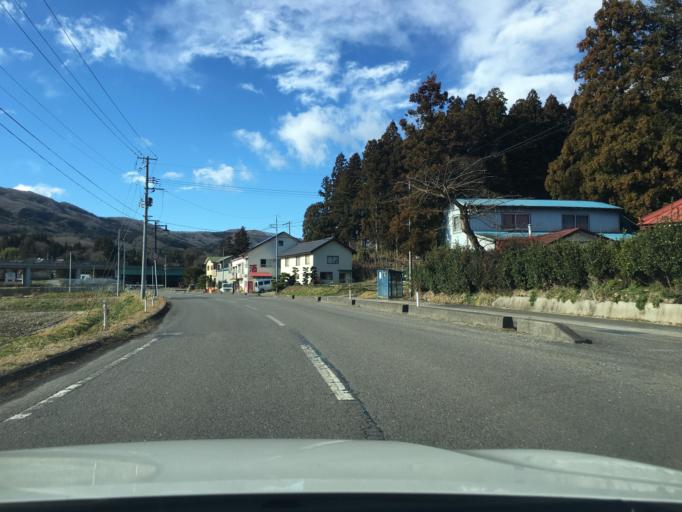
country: JP
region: Fukushima
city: Funehikimachi-funehiki
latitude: 37.3601
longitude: 140.6115
